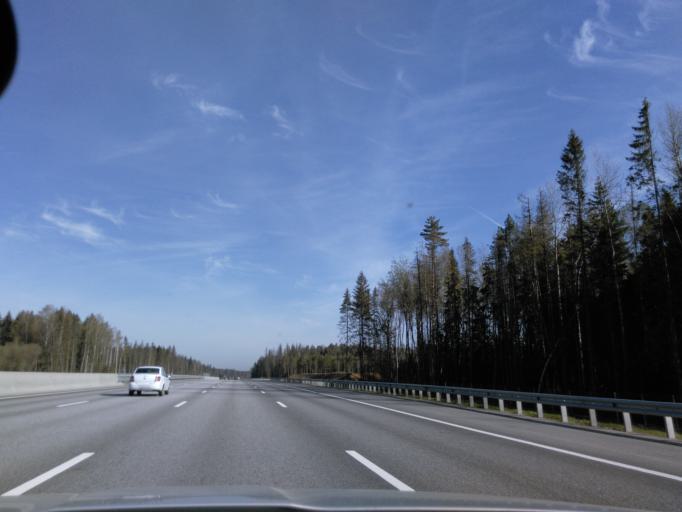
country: RU
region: Moskovskaya
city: Rzhavki
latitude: 56.0126
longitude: 37.2847
